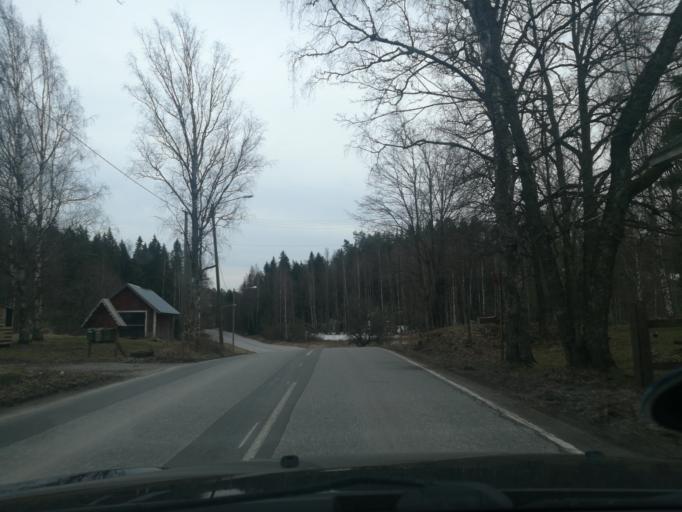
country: FI
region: Uusimaa
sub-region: Helsinki
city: Nickby
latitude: 60.2808
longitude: 25.3725
